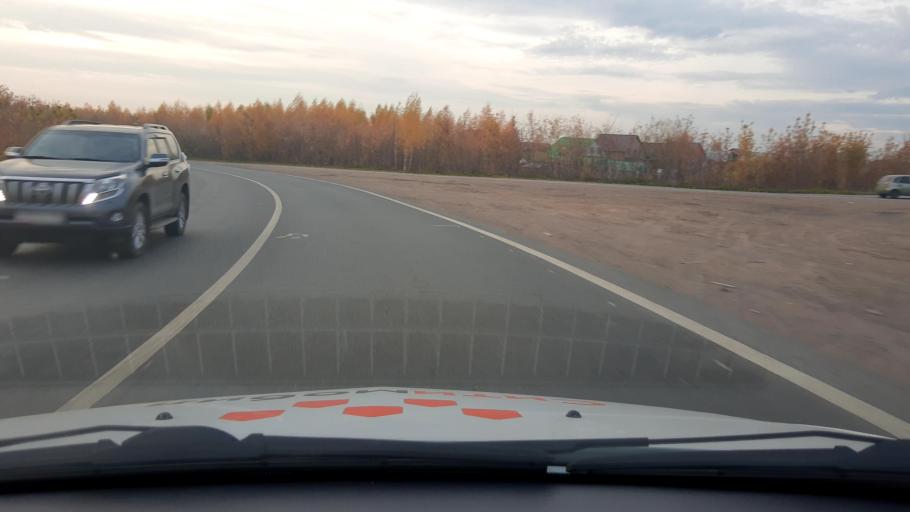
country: RU
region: Bashkortostan
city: Iglino
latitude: 54.7758
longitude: 56.2553
